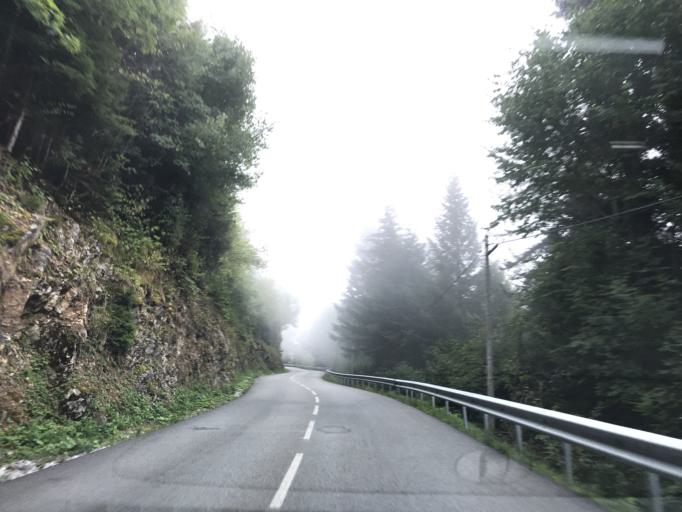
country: FR
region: Rhone-Alpes
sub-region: Departement de la Haute-Savoie
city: Talloires
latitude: 45.8151
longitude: 6.2433
